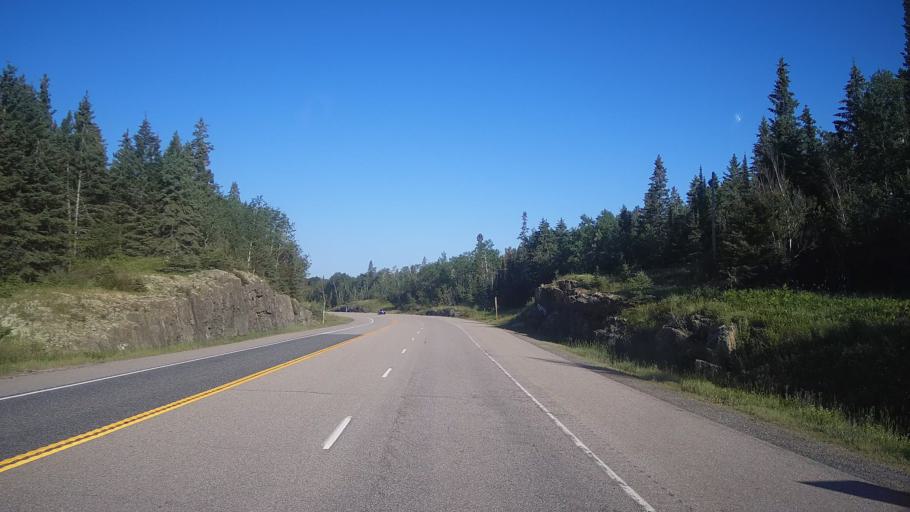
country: US
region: Minnesota
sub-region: Roseau County
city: Warroad
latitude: 49.7185
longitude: -94.7257
